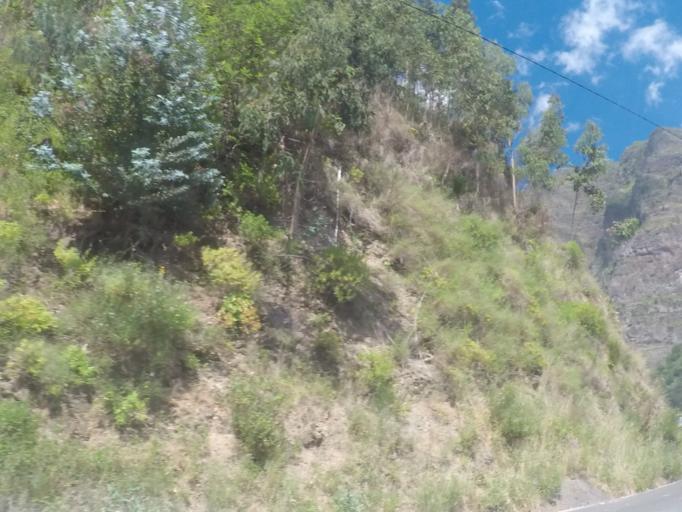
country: PT
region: Madeira
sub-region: Camara de Lobos
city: Curral das Freiras
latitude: 32.7178
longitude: -16.9744
